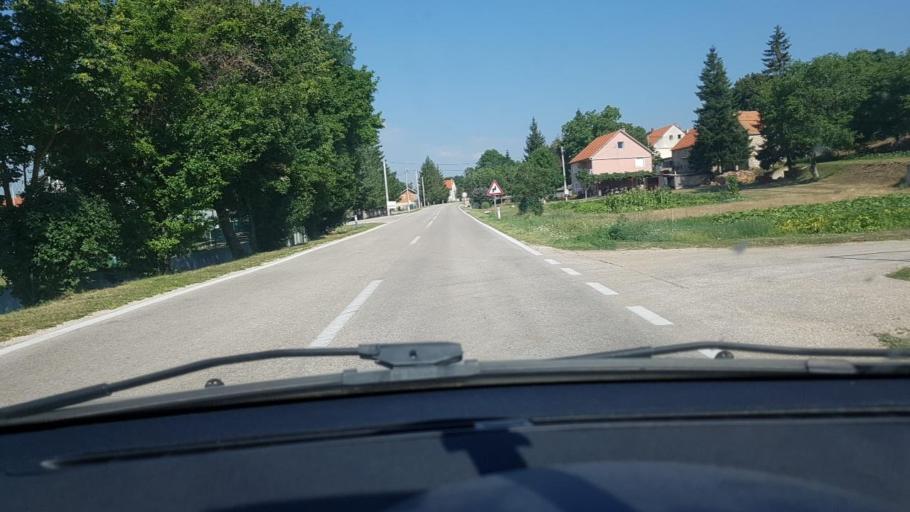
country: BA
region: Federation of Bosnia and Herzegovina
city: Orguz
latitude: 43.8688
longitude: 16.8787
